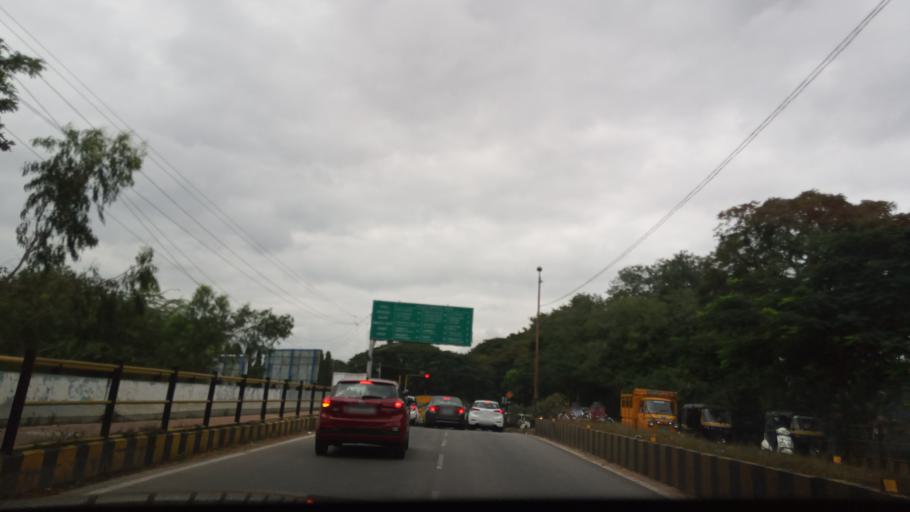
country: IN
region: Karnataka
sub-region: Mysore
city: Mysore
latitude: 12.3121
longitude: 76.6392
